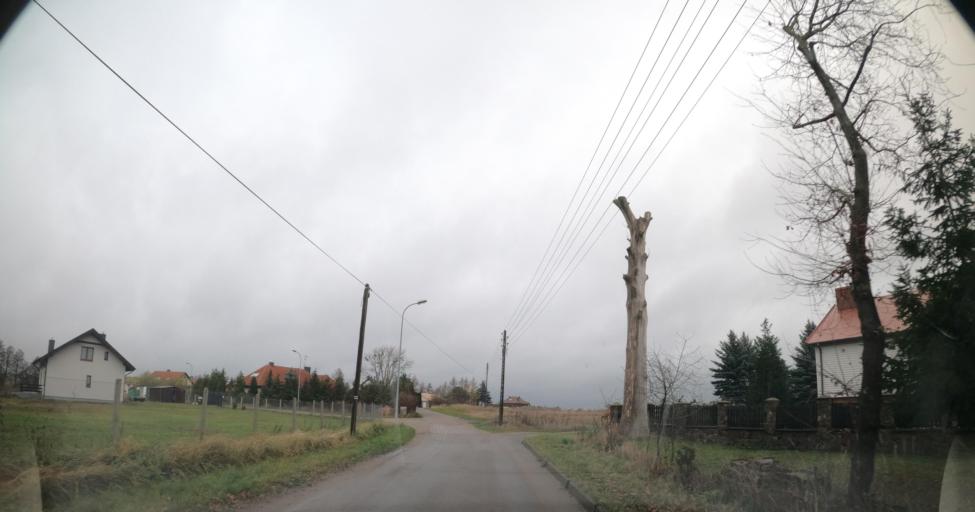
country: PL
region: West Pomeranian Voivodeship
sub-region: Powiat drawski
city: Drawsko Pomorskie
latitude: 53.5356
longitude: 15.8257
